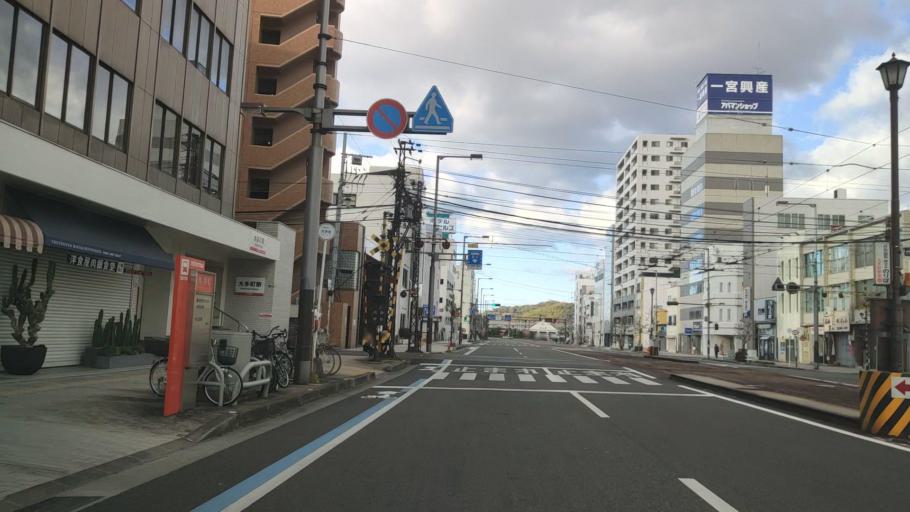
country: JP
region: Ehime
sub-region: Shikoku-chuo Shi
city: Matsuyama
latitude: 33.8401
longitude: 132.7557
